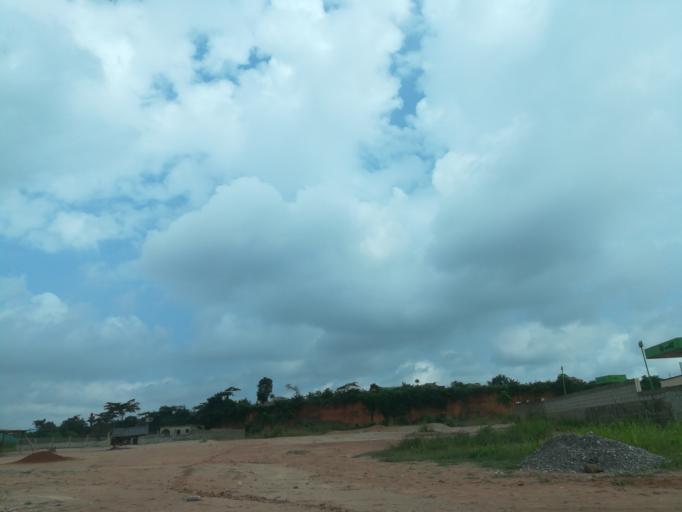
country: NG
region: Lagos
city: Ikorodu
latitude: 6.6591
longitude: 3.5859
